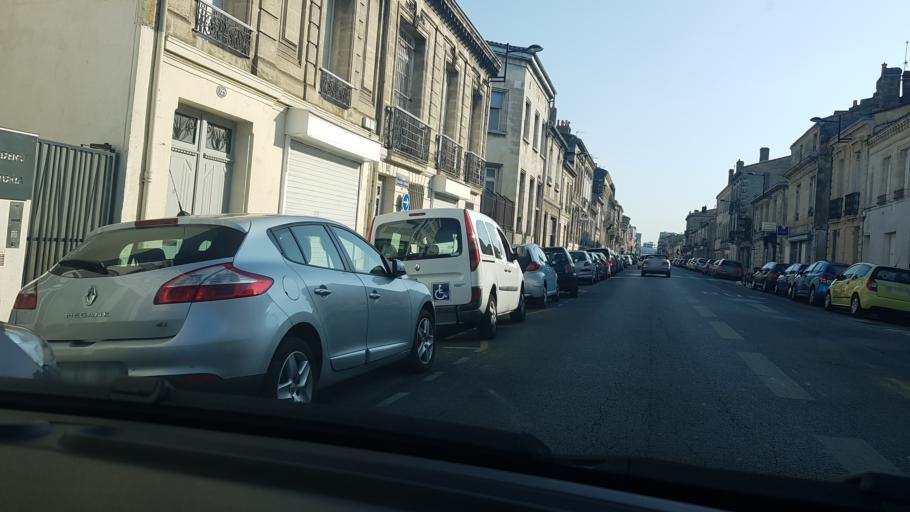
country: FR
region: Aquitaine
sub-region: Departement de la Gironde
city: Bordeaux
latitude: 44.8598
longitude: -0.5648
